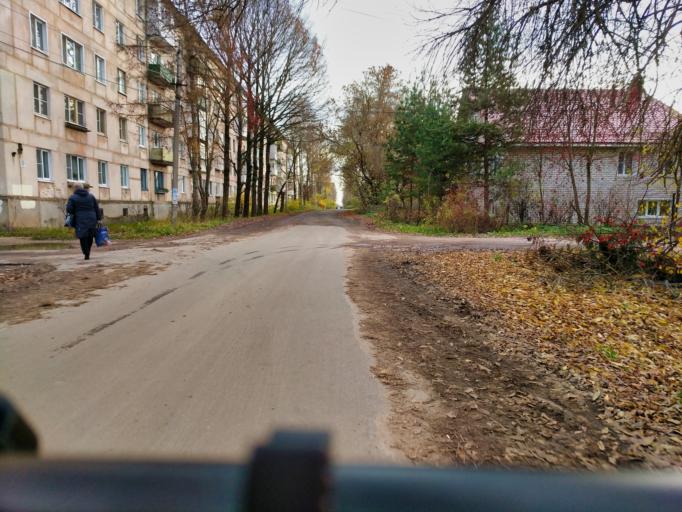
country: RU
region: Tverskaya
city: Rzhev
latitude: 56.2689
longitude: 34.3262
